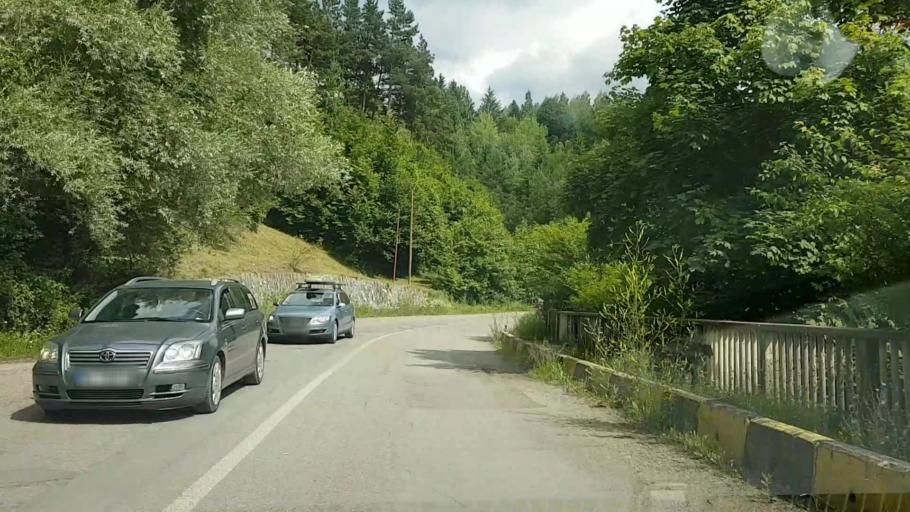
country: RO
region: Neamt
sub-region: Comuna Hangu
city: Hangu
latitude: 47.0512
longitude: 26.0403
